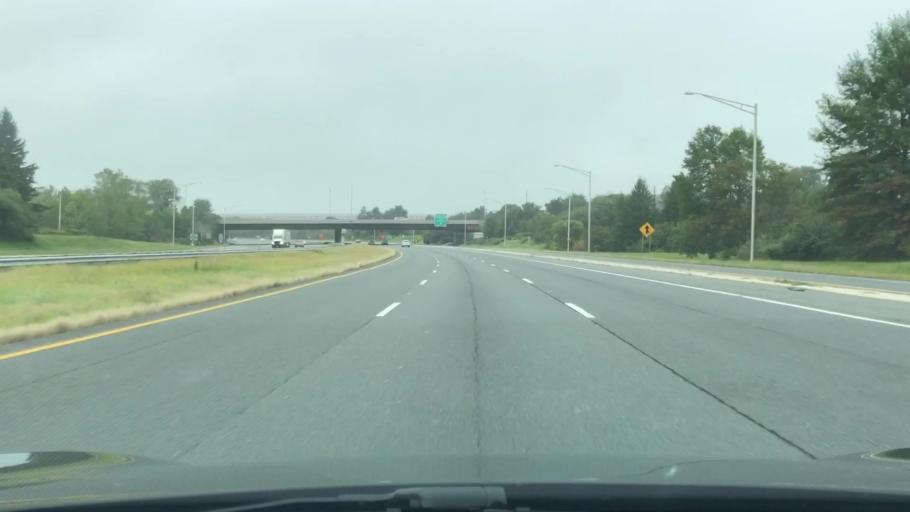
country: US
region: New Jersey
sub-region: Mercer County
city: Ewing
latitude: 40.2898
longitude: -74.8080
